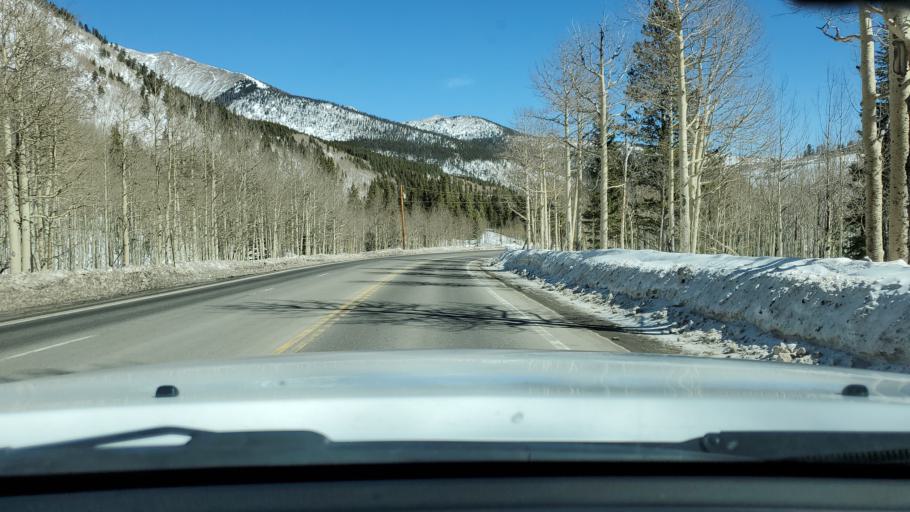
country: US
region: Colorado
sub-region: Chaffee County
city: Salida
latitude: 38.5423
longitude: -106.3140
